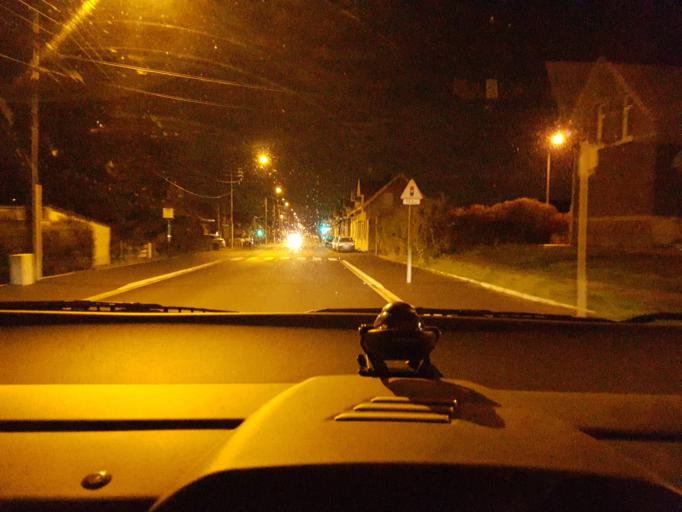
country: FR
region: Nord-Pas-de-Calais
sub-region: Departement du Pas-de-Calais
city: Bully-les-Mines
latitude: 50.4425
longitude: 2.7339
